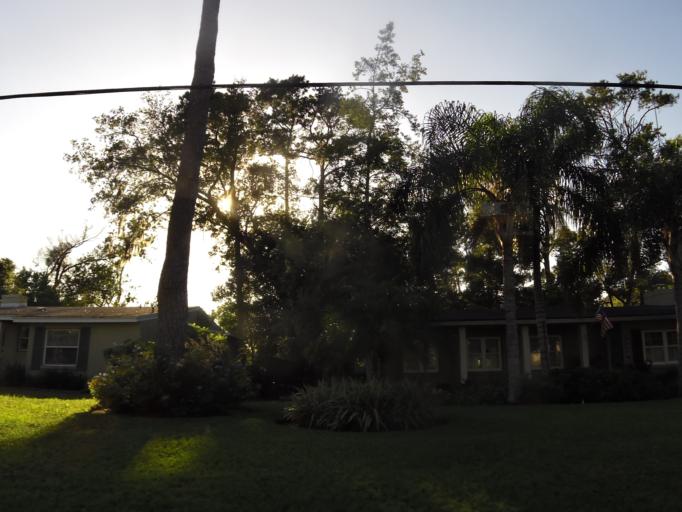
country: US
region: Florida
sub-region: Duval County
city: Jacksonville
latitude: 30.2660
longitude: -81.6434
